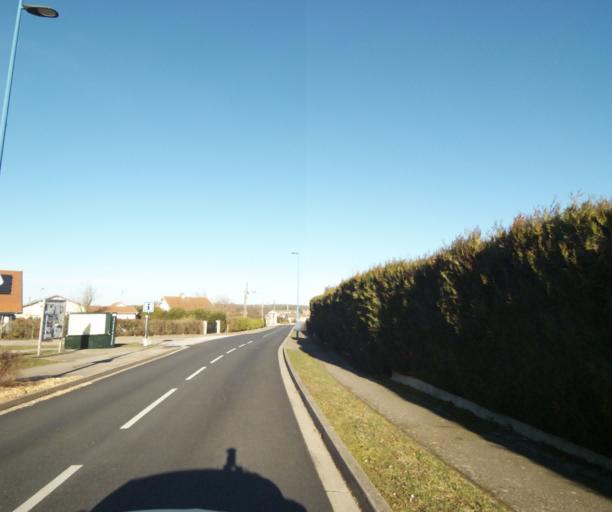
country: FR
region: Lorraine
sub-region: Departement de Meurthe-et-Moselle
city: Heillecourt
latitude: 48.6592
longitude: 6.2171
